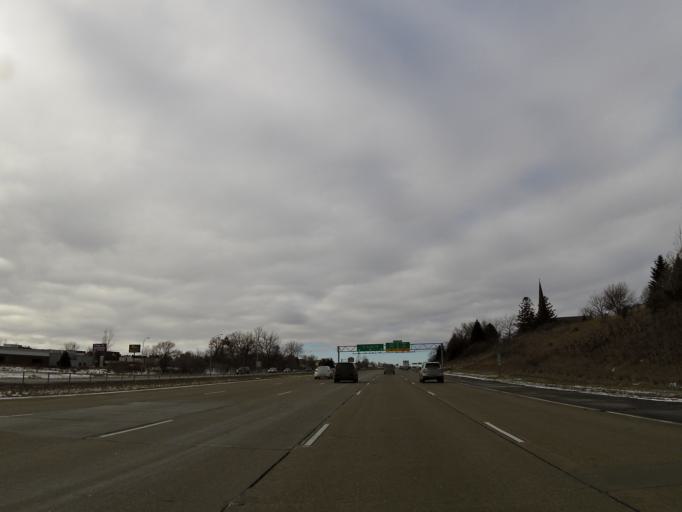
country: US
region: Minnesota
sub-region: Washington County
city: Oakdale
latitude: 44.9487
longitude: -92.9366
